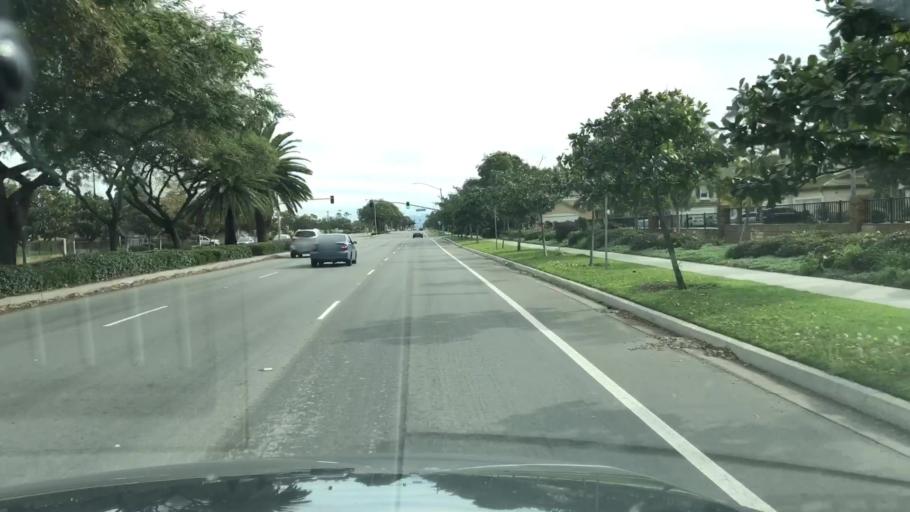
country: US
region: California
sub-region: Ventura County
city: El Rio
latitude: 34.2189
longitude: -119.1669
